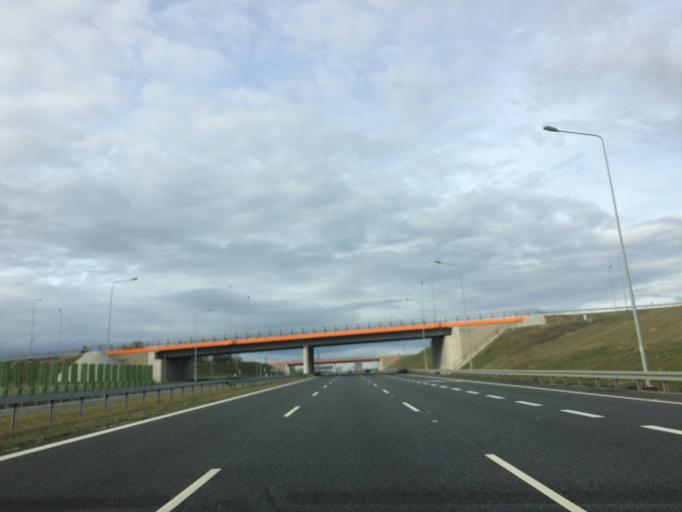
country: PL
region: Lower Silesian Voivodeship
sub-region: Legnica
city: Legnica
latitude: 51.1730
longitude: 16.0945
